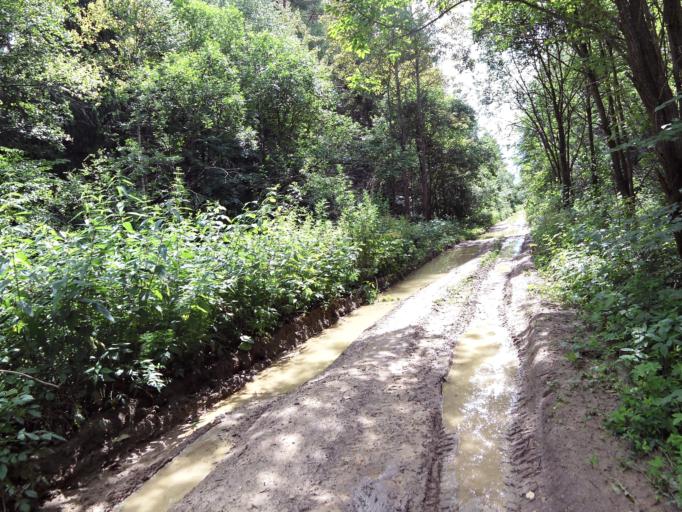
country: RU
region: Moskovskaya
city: Popovo
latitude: 54.9815
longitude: 37.6938
